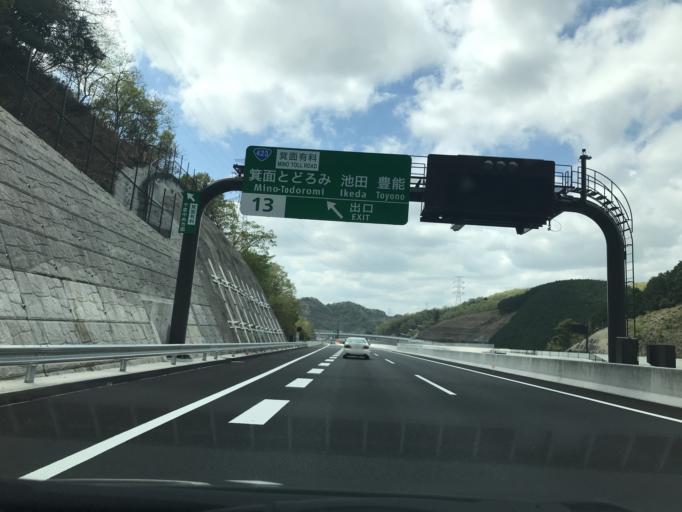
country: JP
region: Osaka
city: Mino
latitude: 34.8769
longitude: 135.4617
